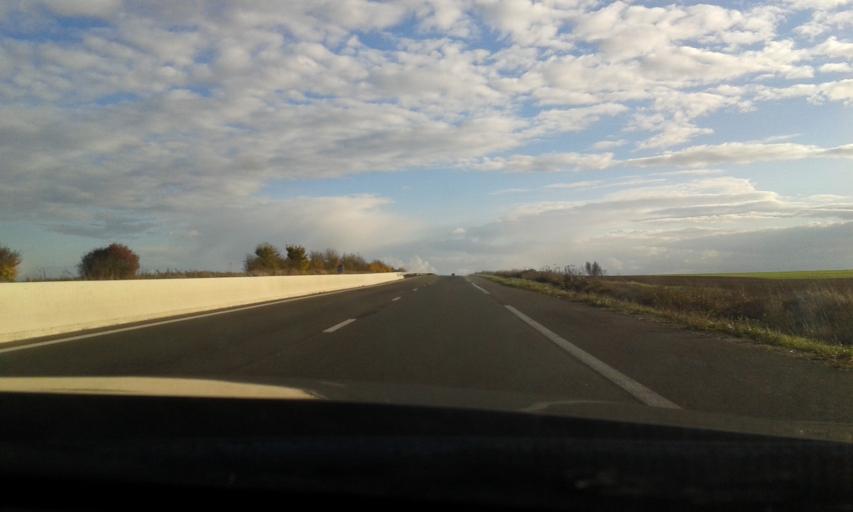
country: FR
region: Centre
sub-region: Departement d'Eure-et-Loir
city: Bailleau-l'Eveque
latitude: 48.5560
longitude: 1.4446
